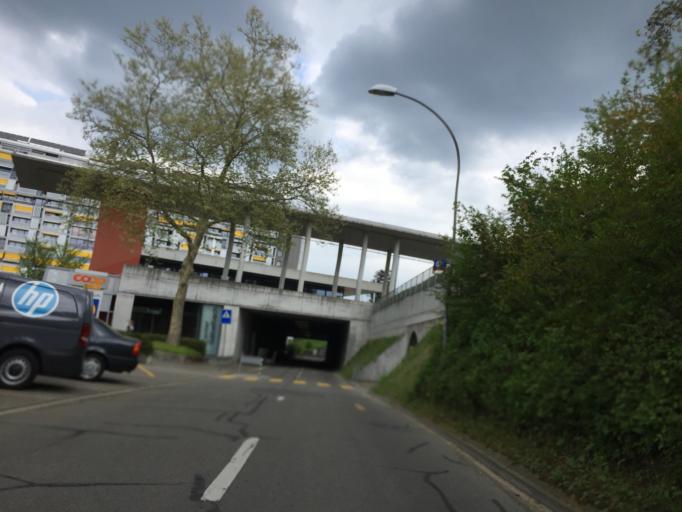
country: CH
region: Bern
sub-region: Bern-Mittelland District
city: Wohlen
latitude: 46.9484
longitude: 7.3760
